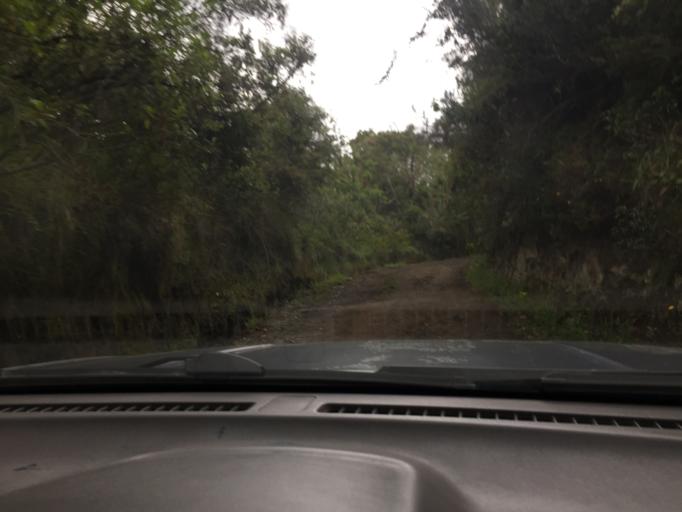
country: EC
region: Imbabura
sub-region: Canton Otavalo
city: Otavalo
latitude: 0.0815
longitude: -78.2971
